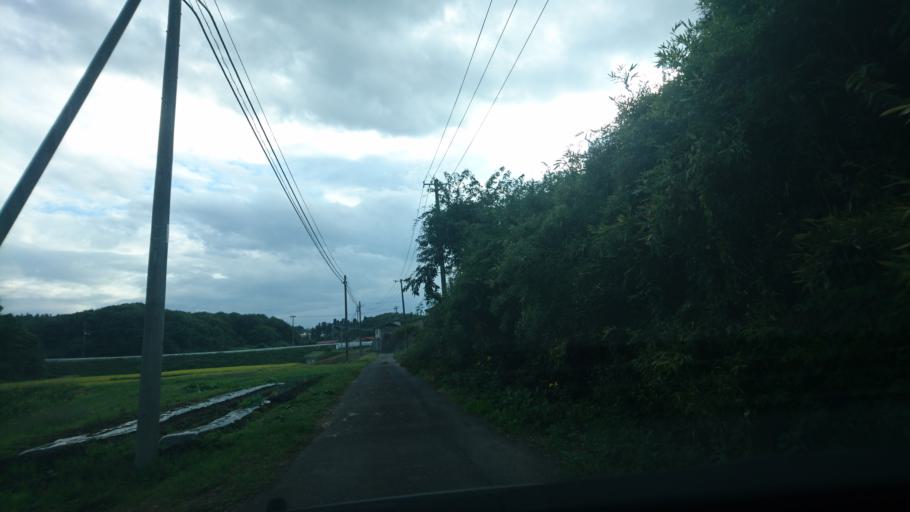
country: JP
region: Iwate
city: Ichinoseki
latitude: 38.8881
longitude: 141.1464
